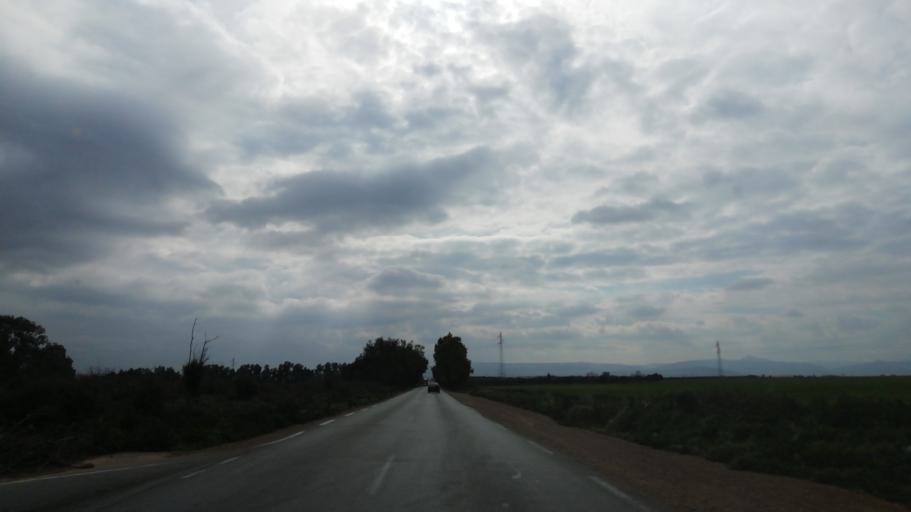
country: DZ
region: Oran
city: Sidi ech Chahmi
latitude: 35.5777
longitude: -0.4518
